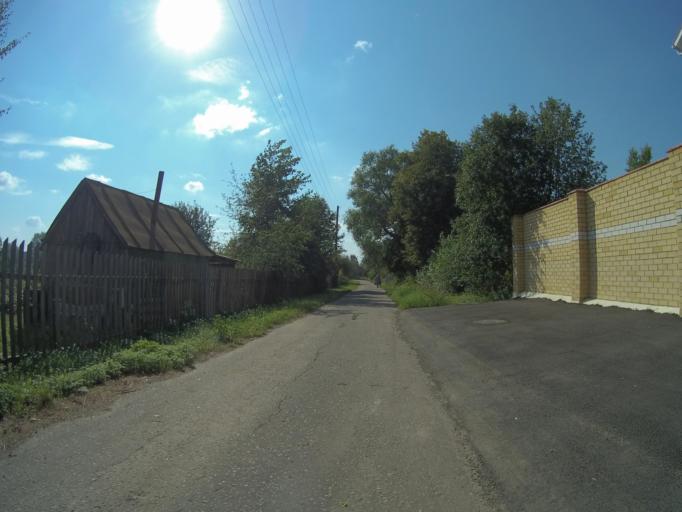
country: RU
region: Vladimir
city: Bogolyubovo
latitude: 56.3040
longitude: 40.5185
